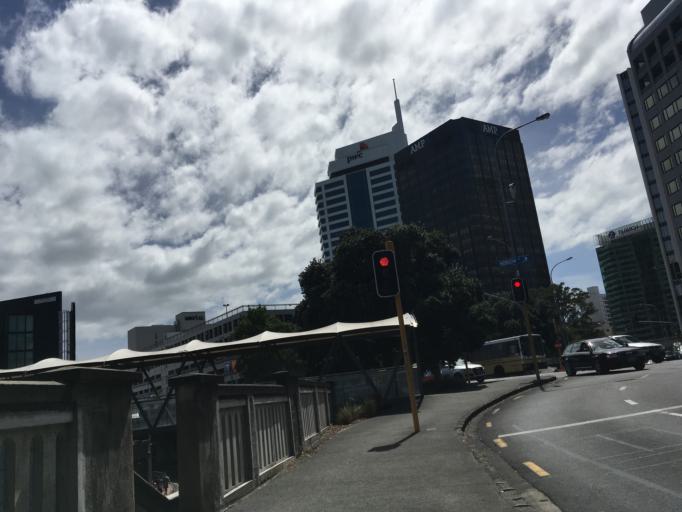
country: NZ
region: Auckland
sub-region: Auckland
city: Auckland
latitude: -36.8445
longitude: 174.7629
